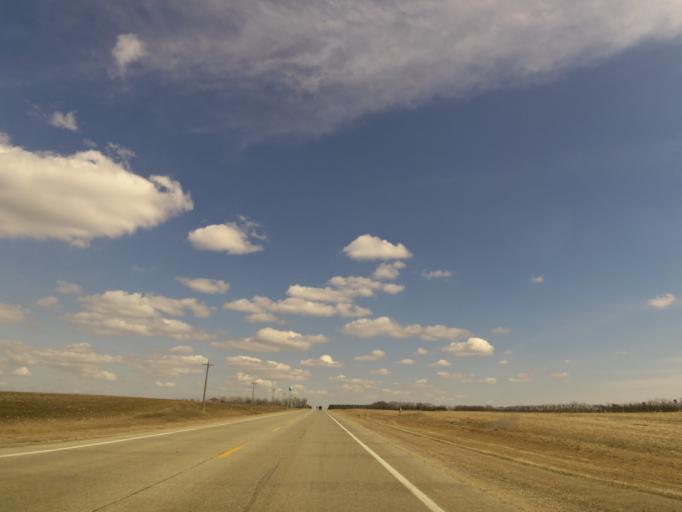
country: US
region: South Dakota
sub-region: Codington County
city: Watertown
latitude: 44.8901
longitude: -96.9792
